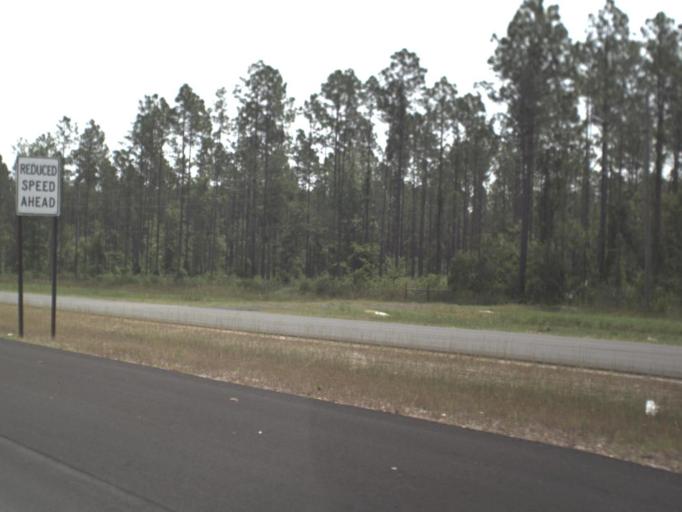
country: US
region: Florida
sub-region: Duval County
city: Baldwin
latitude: 30.3675
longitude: -81.9454
